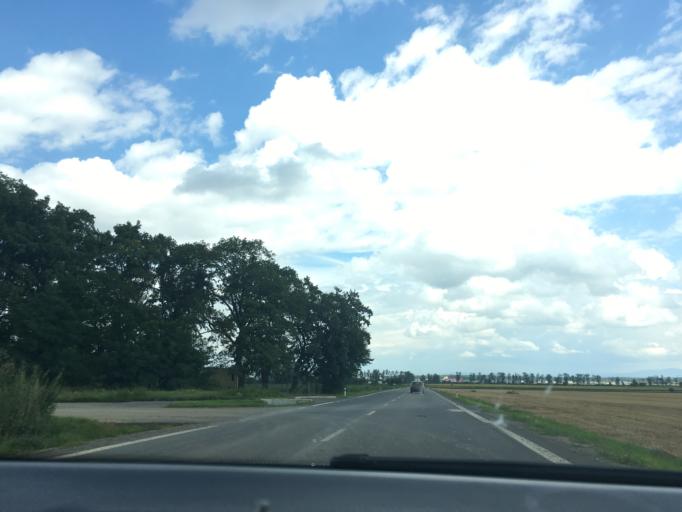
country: SK
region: Kosicky
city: Trebisov
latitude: 48.5914
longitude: 21.7110
